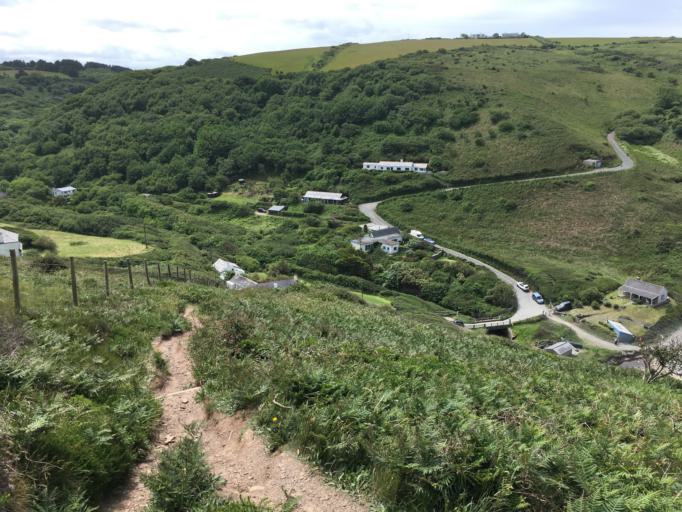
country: GB
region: England
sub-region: Cornwall
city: Poundstock
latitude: 50.7723
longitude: -4.5744
